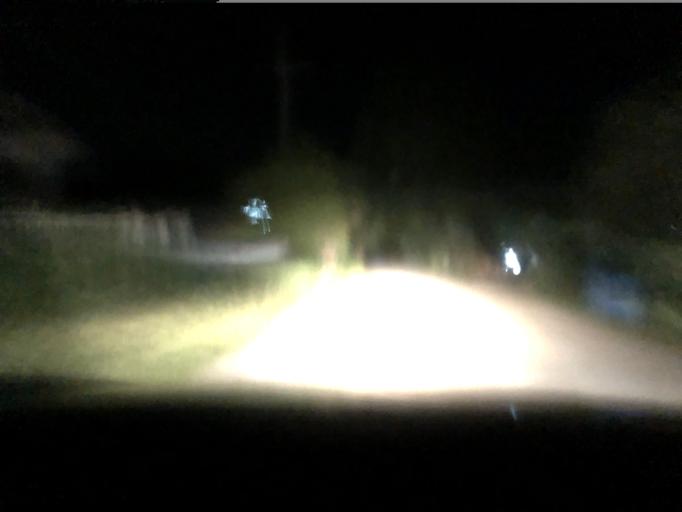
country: TH
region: Nakhon Sawan
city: Takhli
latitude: 15.2576
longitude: 100.3330
